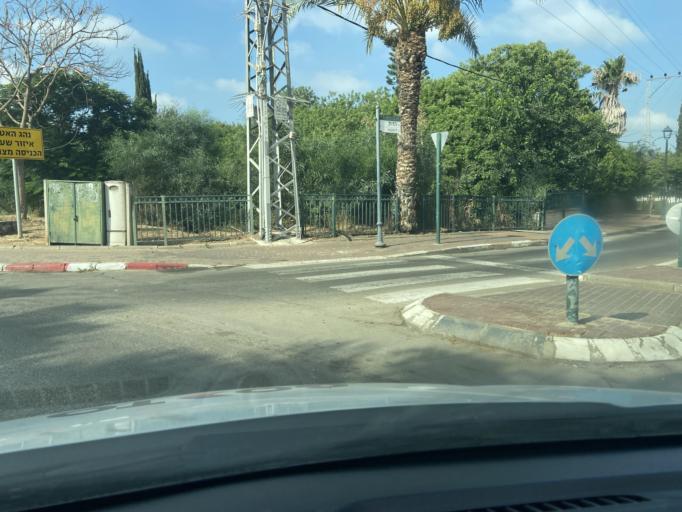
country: IL
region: Central District
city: Yehud
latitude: 32.0404
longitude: 34.8830
